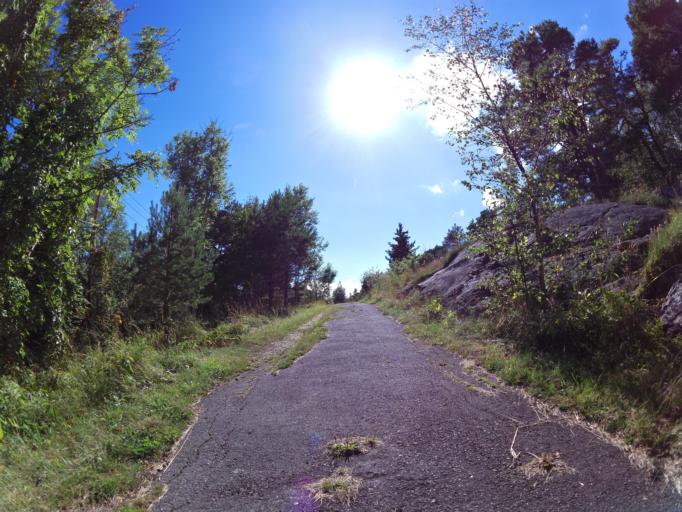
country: NO
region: Ostfold
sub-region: Fredrikstad
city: Fredrikstad
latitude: 59.1723
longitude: 10.8447
